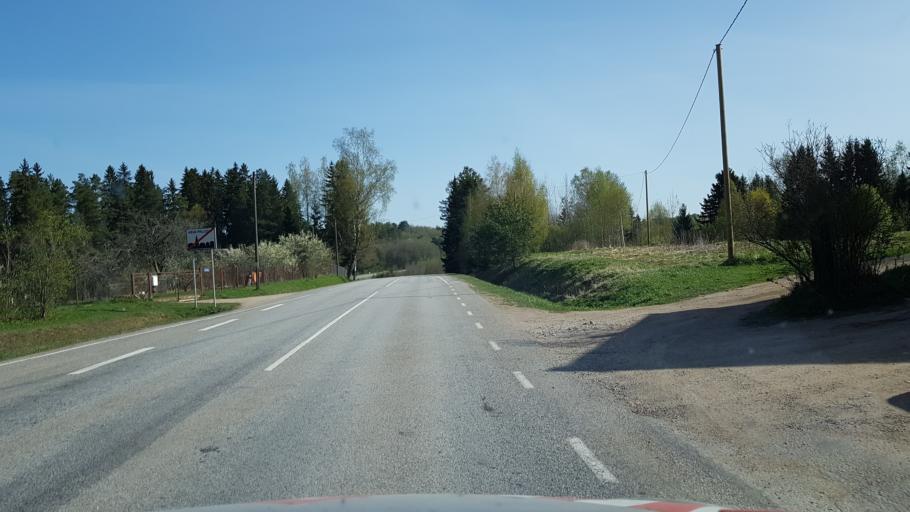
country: EE
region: Viljandimaa
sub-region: Abja vald
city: Abja-Paluoja
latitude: 58.1356
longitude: 25.3685
